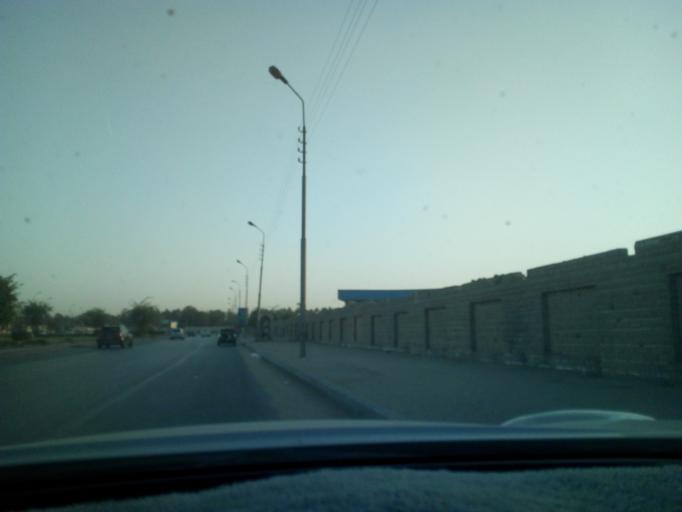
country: EG
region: Muhafazat al Qalyubiyah
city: Al Khankah
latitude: 30.1198
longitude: 31.3637
